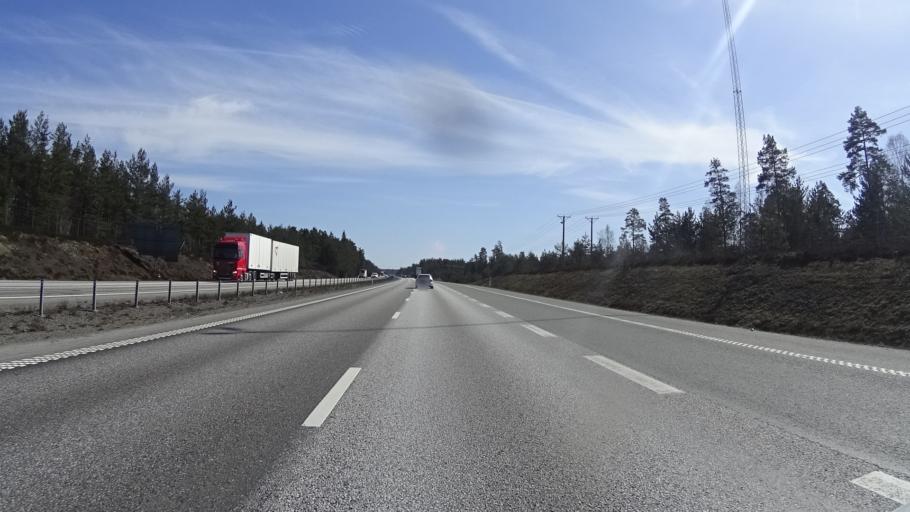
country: SE
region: Joenkoeping
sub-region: Jonkopings Kommun
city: Odensjo
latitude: 57.6864
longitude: 14.1614
